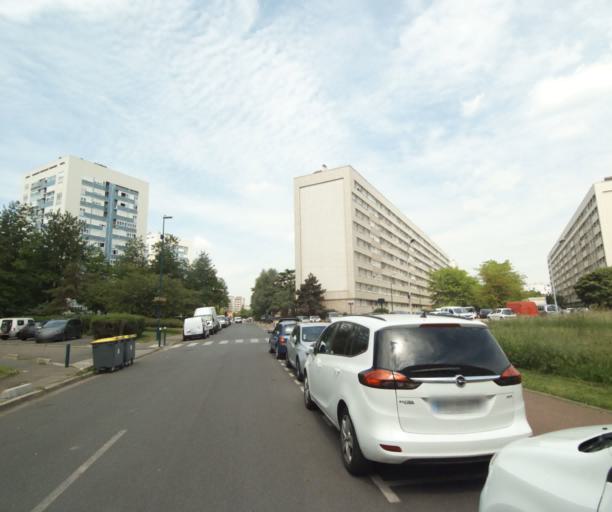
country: FR
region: Ile-de-France
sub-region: Departement des Hauts-de-Seine
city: Asnieres-sur-Seine
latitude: 48.9199
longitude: 2.2912
